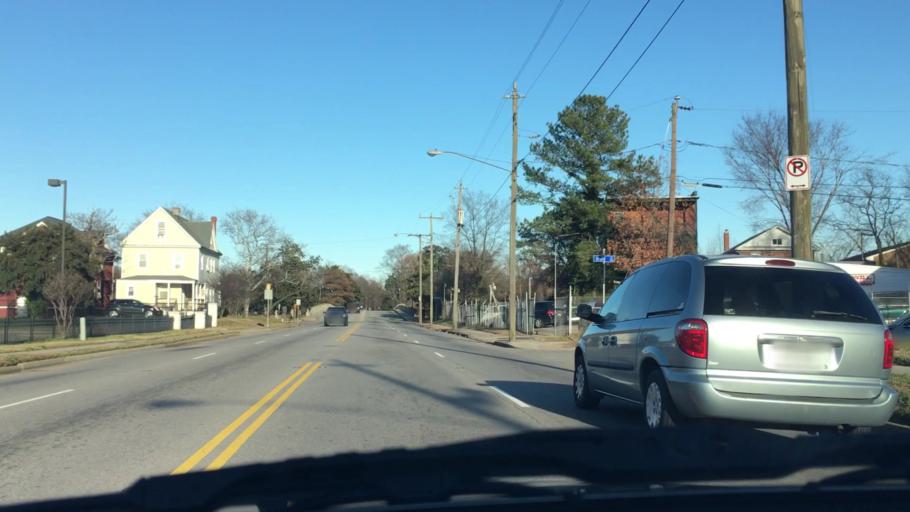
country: US
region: Virginia
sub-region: City of Norfolk
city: Norfolk
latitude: 36.8724
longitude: -76.2743
